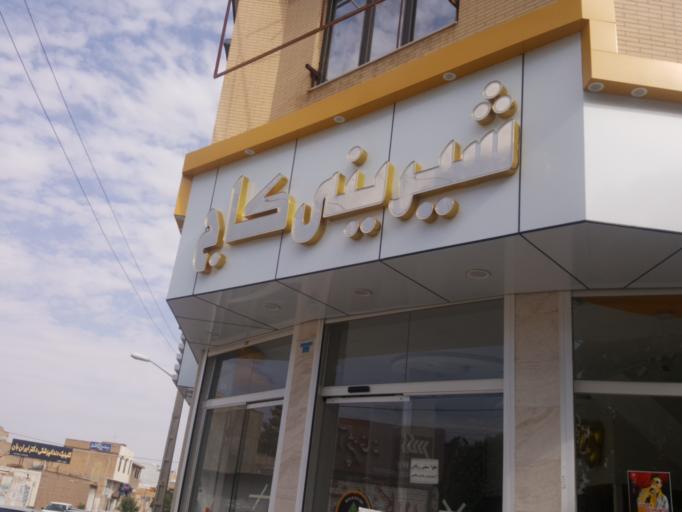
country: IR
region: Fars
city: Marvdasht
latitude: 29.8831
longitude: 52.8107
